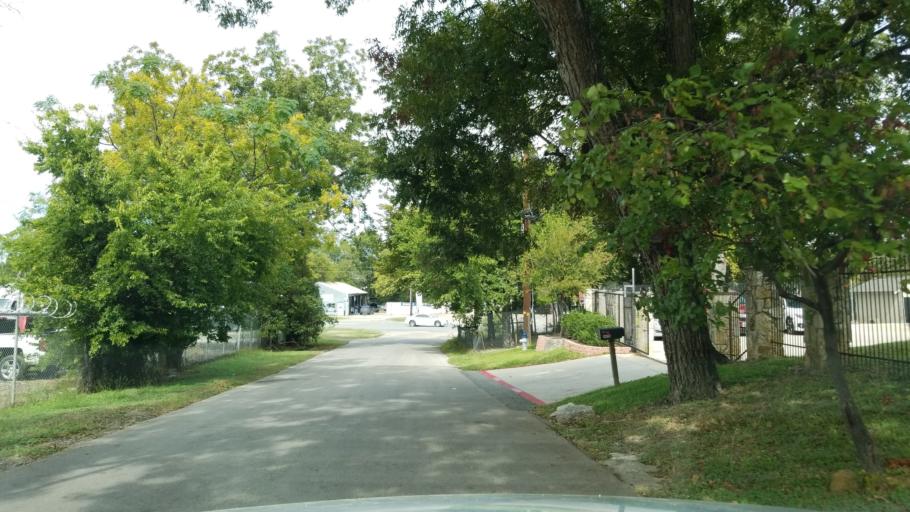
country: US
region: Texas
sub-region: Dallas County
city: Dallas
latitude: 32.7824
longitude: -96.7265
